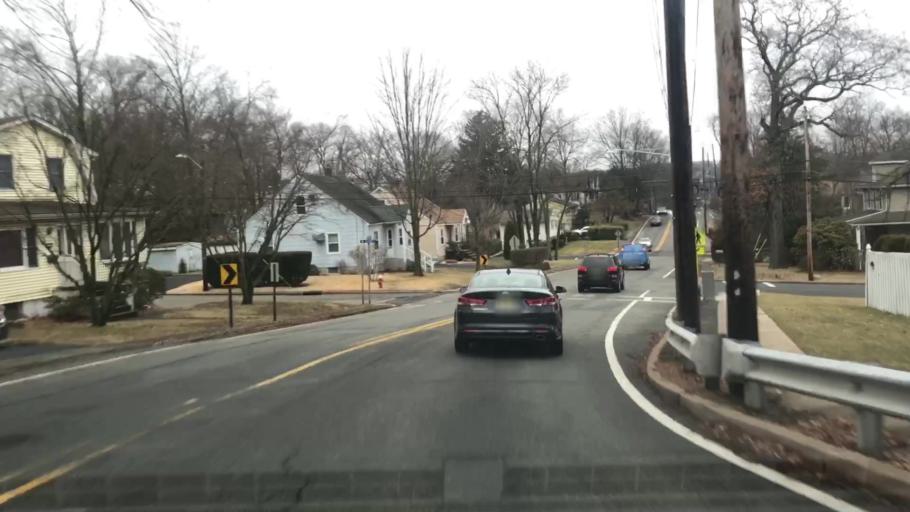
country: US
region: New Jersey
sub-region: Bergen County
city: Hillsdale
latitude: 40.9953
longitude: -74.0494
